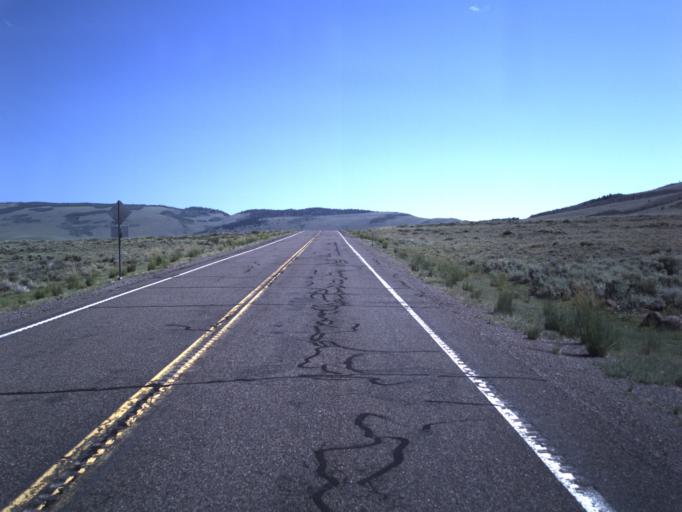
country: US
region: Utah
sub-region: Wayne County
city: Loa
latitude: 38.5523
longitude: -111.5085
